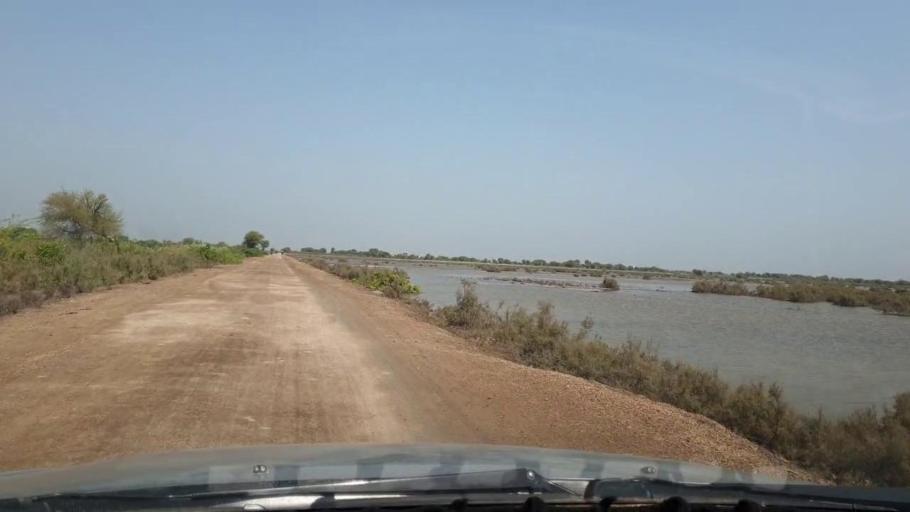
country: PK
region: Sindh
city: Tando Muhammad Khan
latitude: 25.1401
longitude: 68.6317
